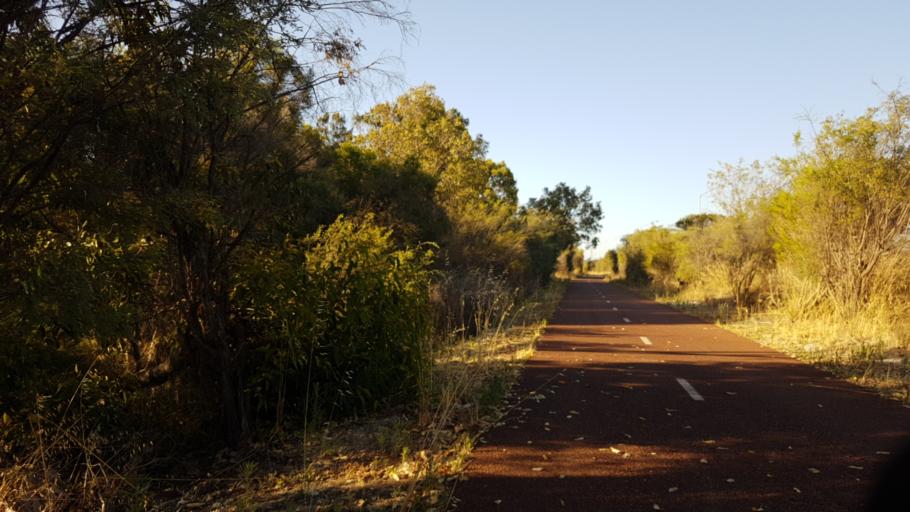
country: AU
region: Western Australia
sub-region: Kwinana
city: Bertram
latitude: -32.2486
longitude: 115.8522
